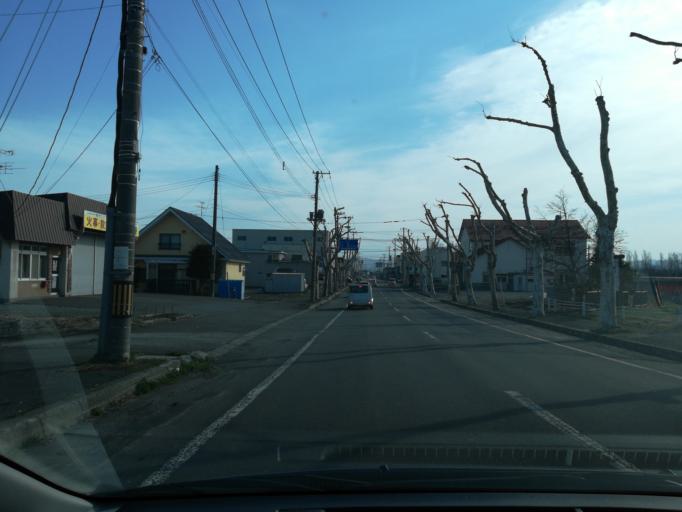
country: JP
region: Hokkaido
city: Iwamizawa
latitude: 43.2089
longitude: 141.7598
